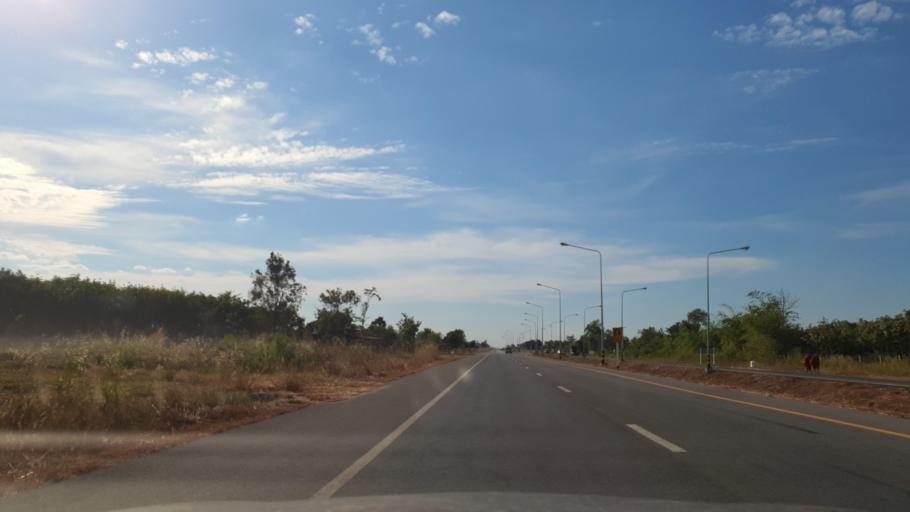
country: TH
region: Kalasin
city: Don Chan
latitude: 16.4109
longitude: 103.7387
